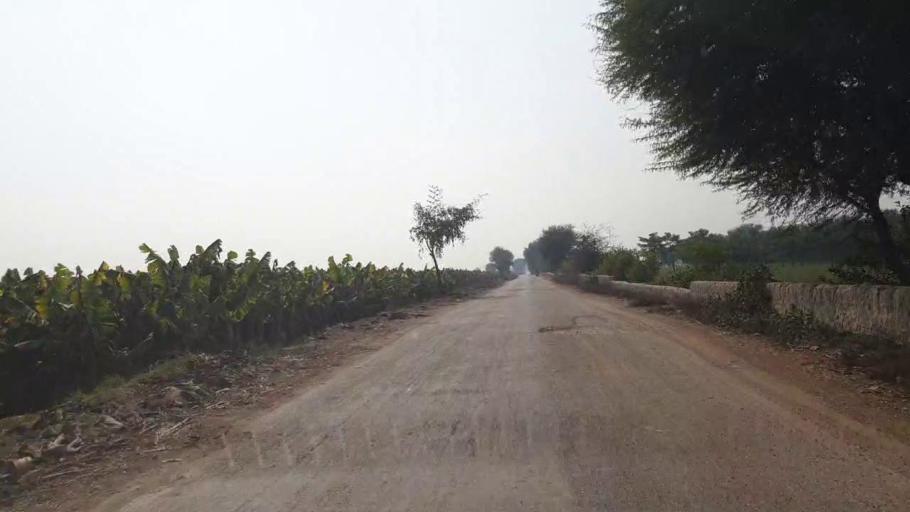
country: PK
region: Sindh
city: Hala
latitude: 25.8545
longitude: 68.4212
